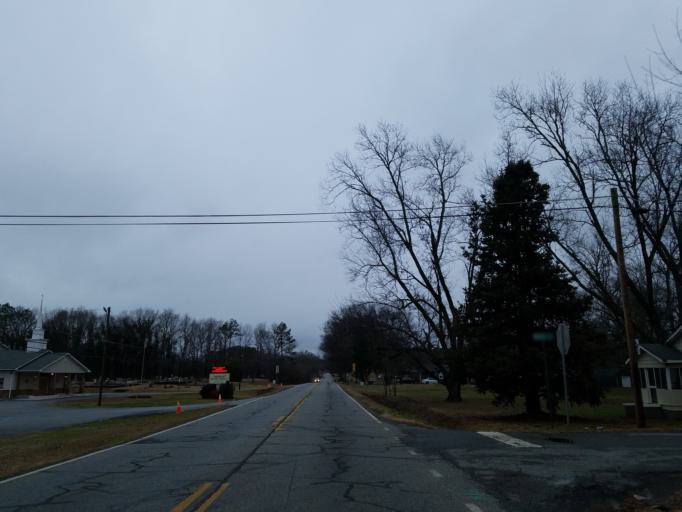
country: US
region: Georgia
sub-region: Bartow County
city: Cartersville
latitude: 34.1974
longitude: -84.8253
